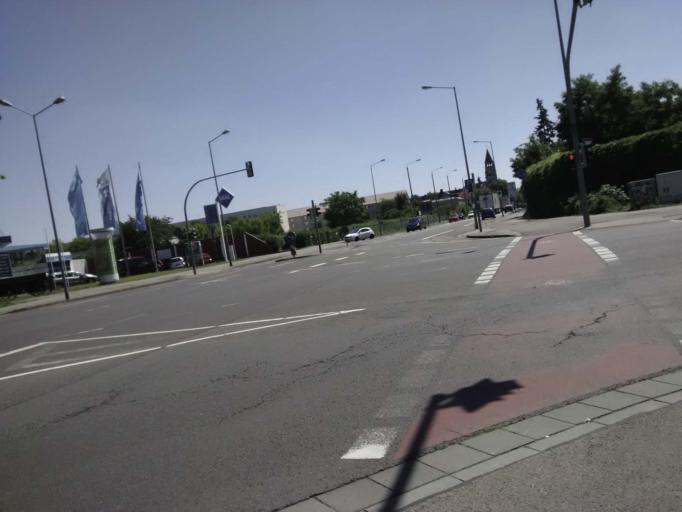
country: DE
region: Saxony-Anhalt
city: Dessau
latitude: 51.8486
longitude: 12.2409
